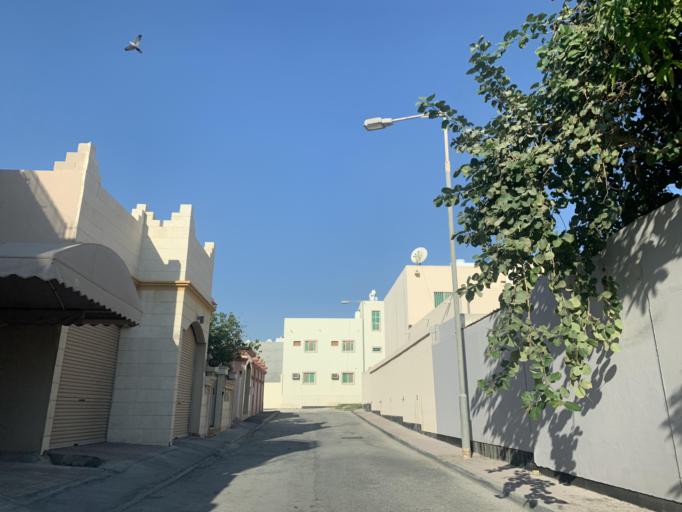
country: BH
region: Central Governorate
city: Madinat Hamad
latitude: 26.1088
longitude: 50.5081
